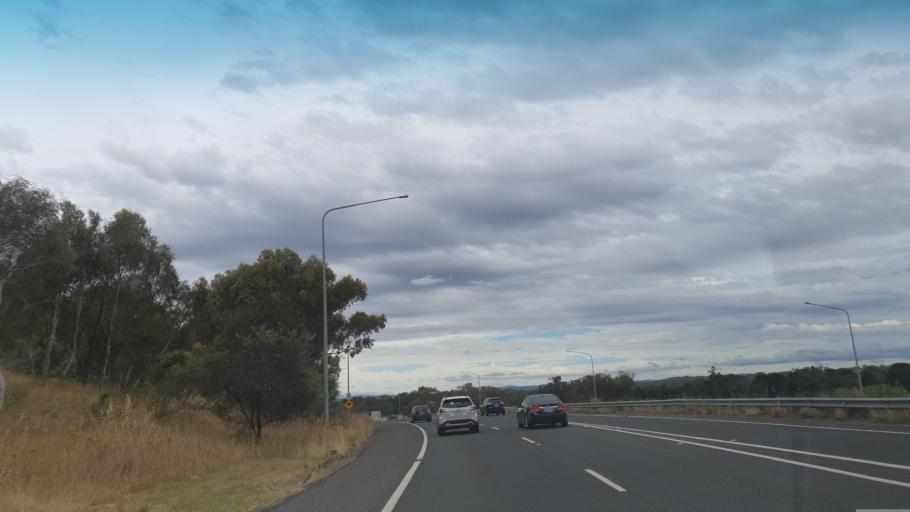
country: AU
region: Australian Capital Territory
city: Acton
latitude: -35.2847
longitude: 149.0899
